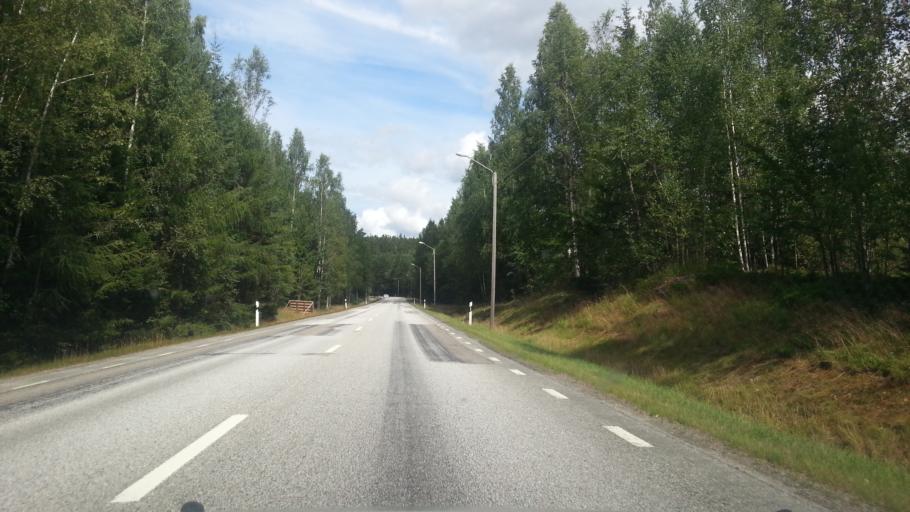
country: SE
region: Vaestmanland
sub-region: Skinnskattebergs Kommun
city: Skinnskatteberg
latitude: 59.8173
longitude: 15.5305
